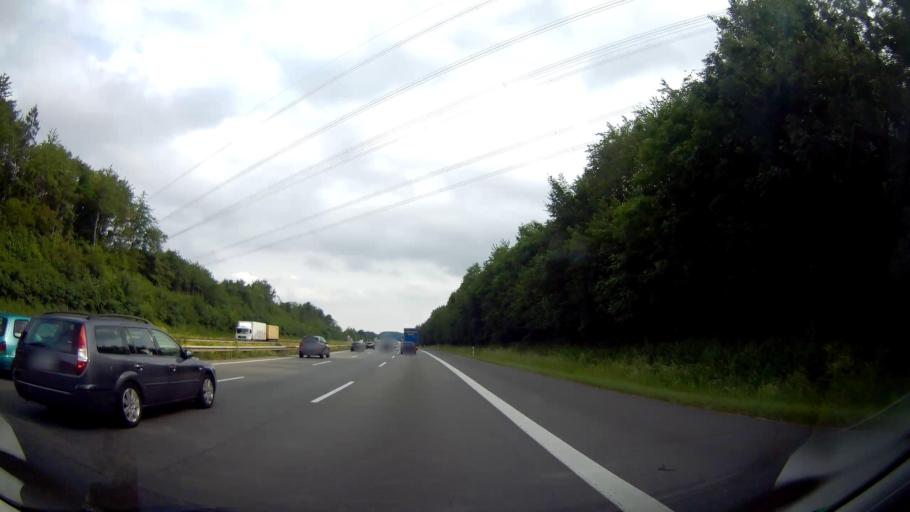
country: DE
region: North Rhine-Westphalia
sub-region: Regierungsbezirk Detmold
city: Leopoldshohe
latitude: 52.0443
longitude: 8.6521
